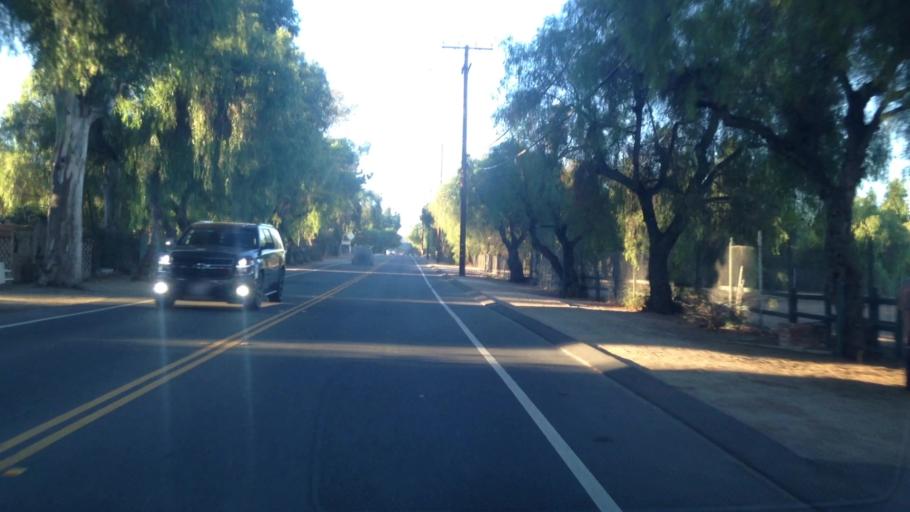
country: US
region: California
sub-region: Riverside County
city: Woodcrest
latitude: 33.8789
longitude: -117.3662
